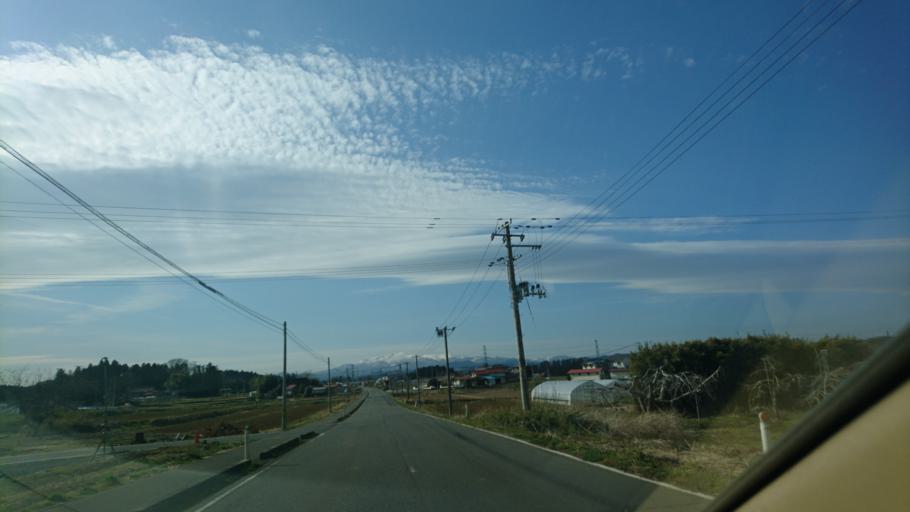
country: JP
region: Iwate
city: Ichinoseki
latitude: 38.8049
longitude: 141.0411
